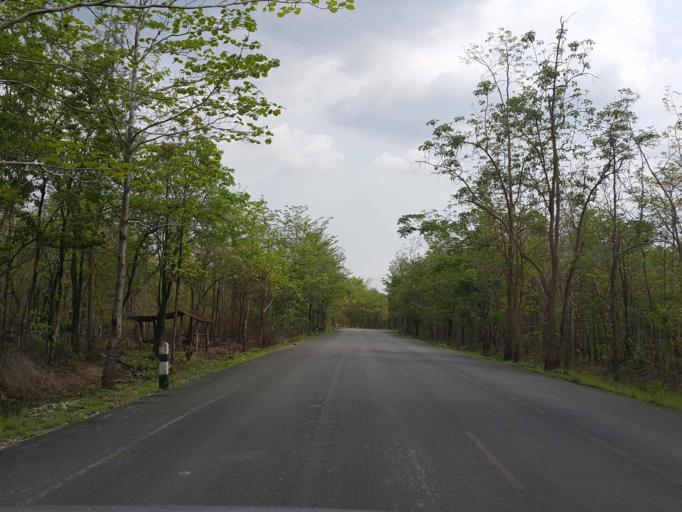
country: TH
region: Sukhothai
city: Thung Saliam
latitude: 17.4460
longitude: 99.3720
